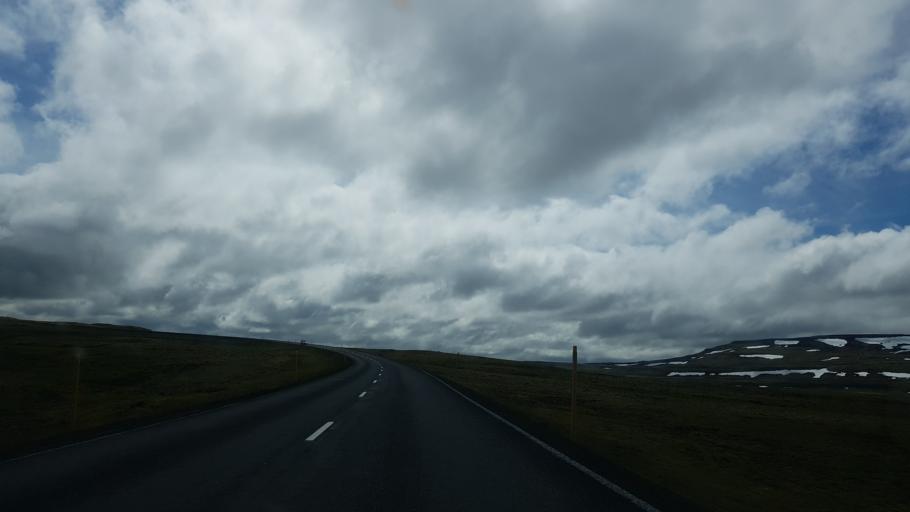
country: IS
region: West
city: Borgarnes
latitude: 65.0021
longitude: -21.0675
